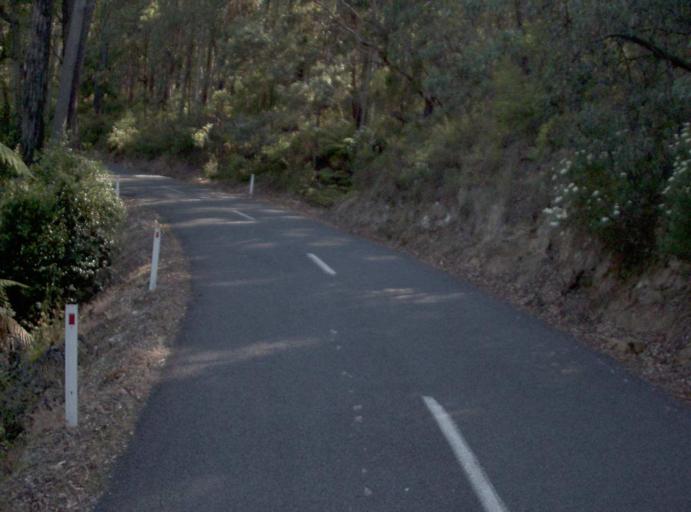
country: AU
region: Victoria
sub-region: East Gippsland
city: Lakes Entrance
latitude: -37.4546
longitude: 148.5763
